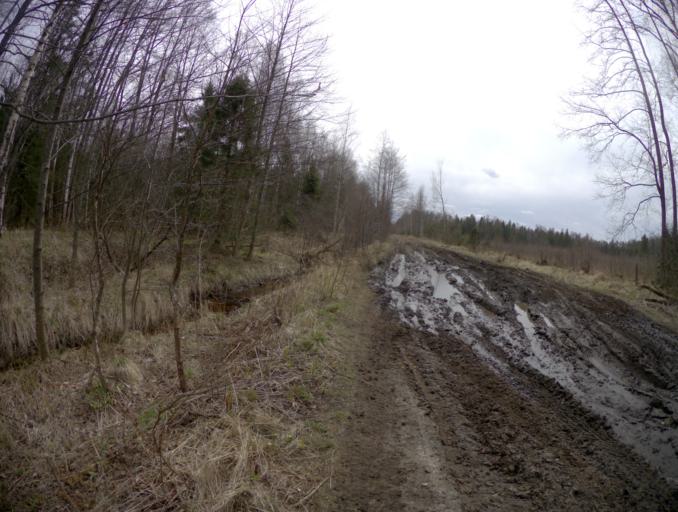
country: RU
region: Vladimir
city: Raduzhnyy
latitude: 55.9389
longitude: 40.2415
